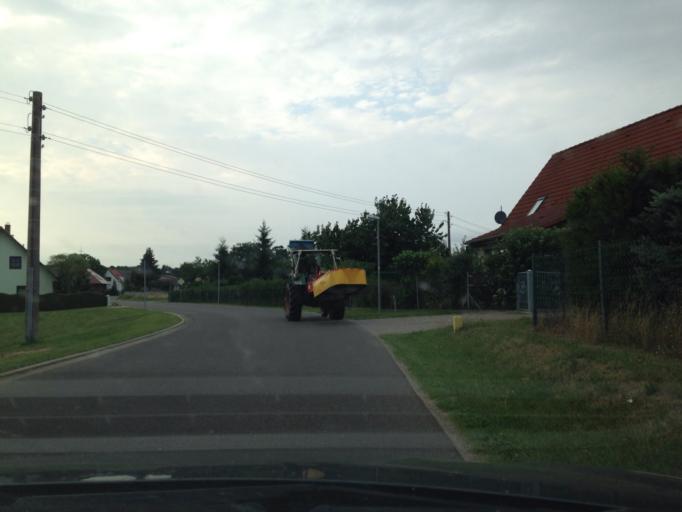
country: DE
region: Mecklenburg-Vorpommern
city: Loitz
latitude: 53.3182
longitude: 13.4165
